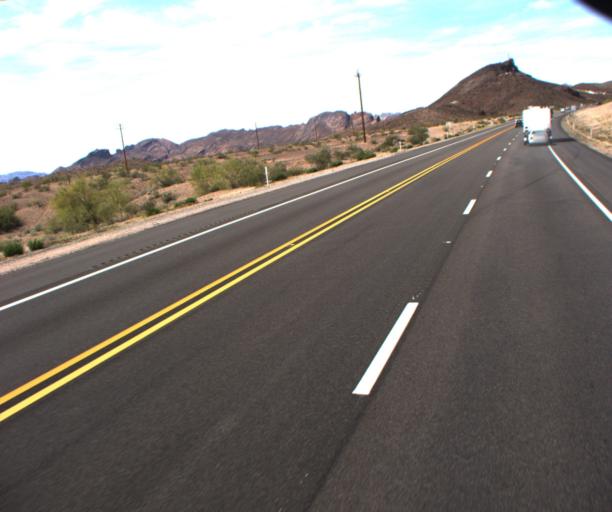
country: US
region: Arizona
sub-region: Mohave County
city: Desert Hills
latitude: 34.5887
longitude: -114.3696
